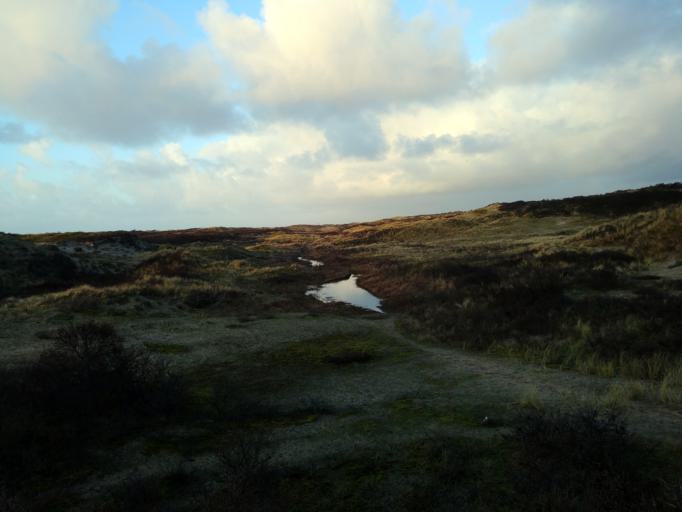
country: NL
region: South Holland
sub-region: Gemeente Noordwijkerhout
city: Noordwijkerhout
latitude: 52.3107
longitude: 4.4924
